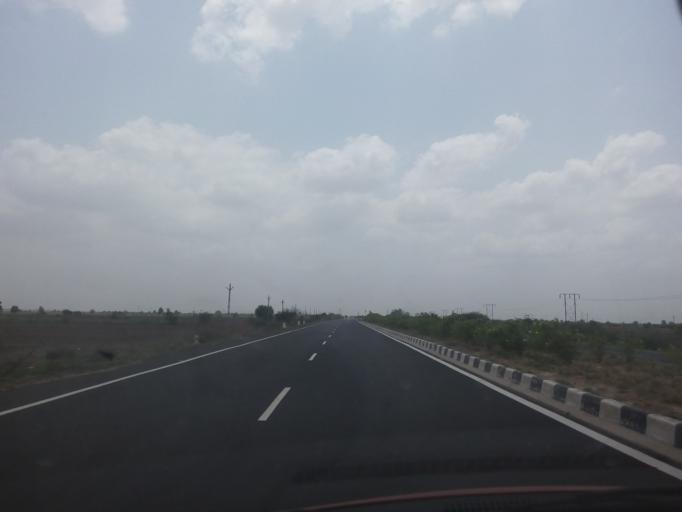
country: IN
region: Gujarat
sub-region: Ahmadabad
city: Mandal
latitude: 23.0868
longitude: 72.0116
